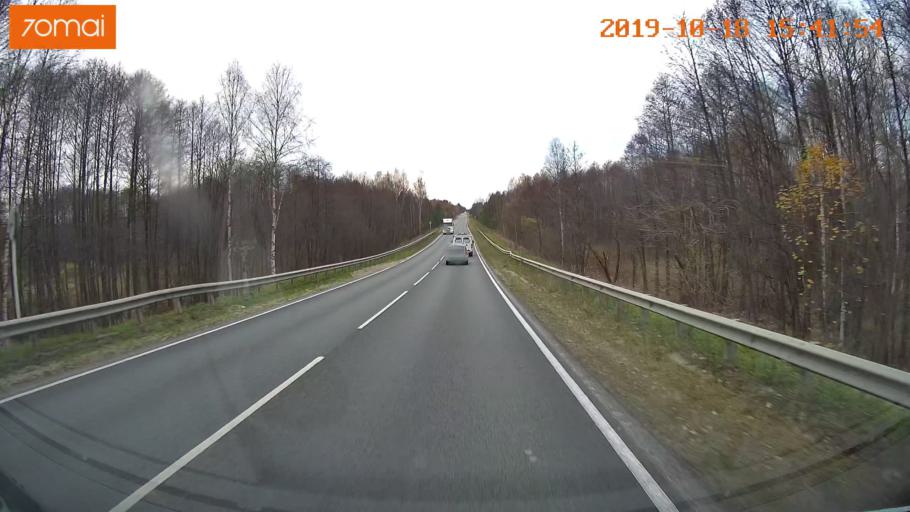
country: RU
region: Vladimir
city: Golovino
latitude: 55.9503
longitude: 40.5760
